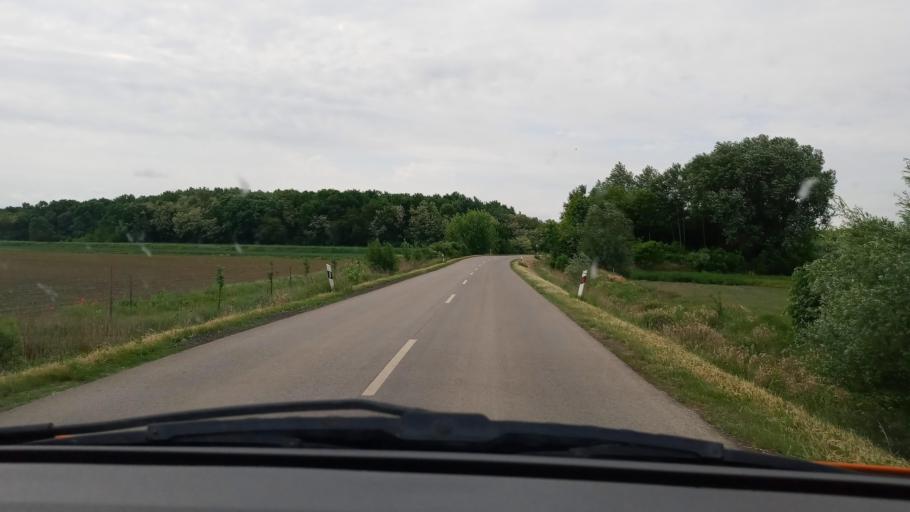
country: HU
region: Baranya
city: Vajszlo
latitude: 45.8976
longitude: 18.0403
